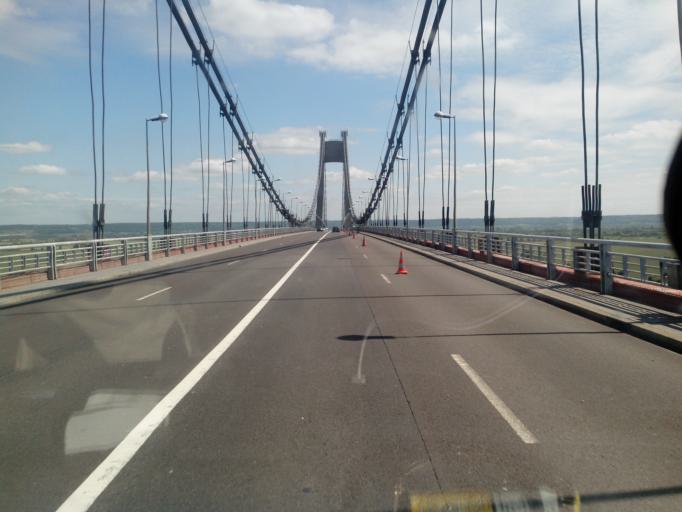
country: FR
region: Haute-Normandie
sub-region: Departement de la Seine-Maritime
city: Tancarville
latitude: 49.4741
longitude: 0.4628
